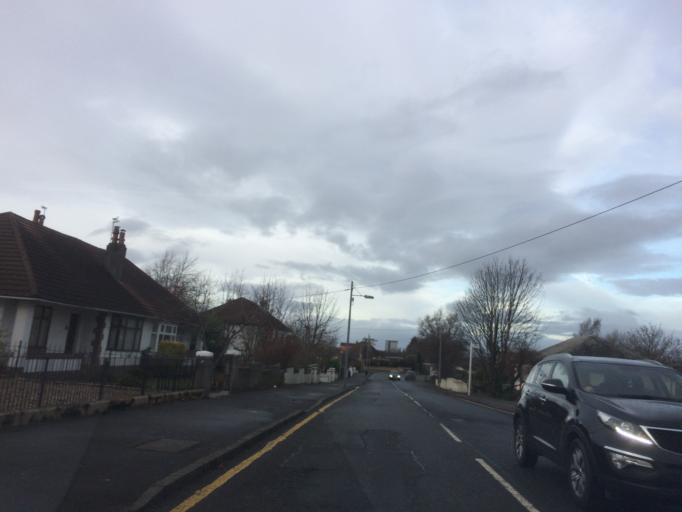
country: GB
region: Scotland
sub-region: East Renfrewshire
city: Giffnock
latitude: 55.8068
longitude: -4.2967
